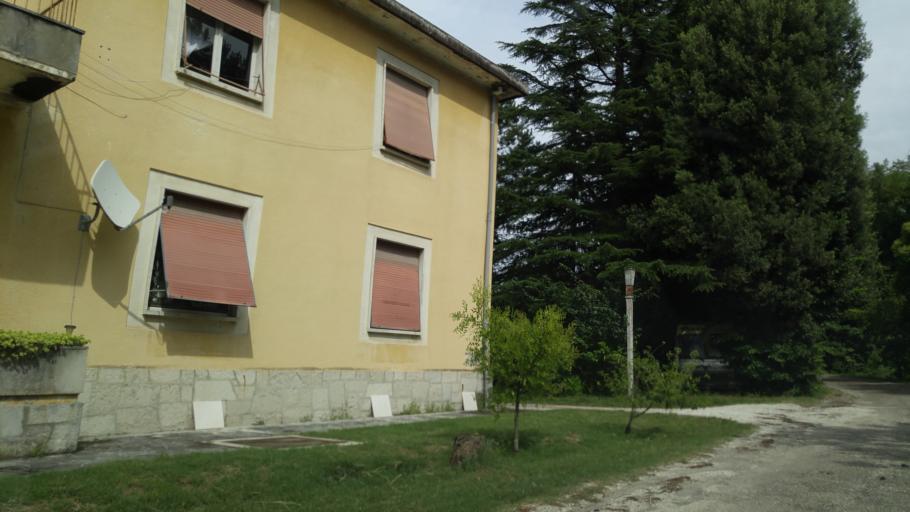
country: IT
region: The Marches
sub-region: Provincia di Pesaro e Urbino
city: Fossombrone
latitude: 43.6677
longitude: 12.7566
